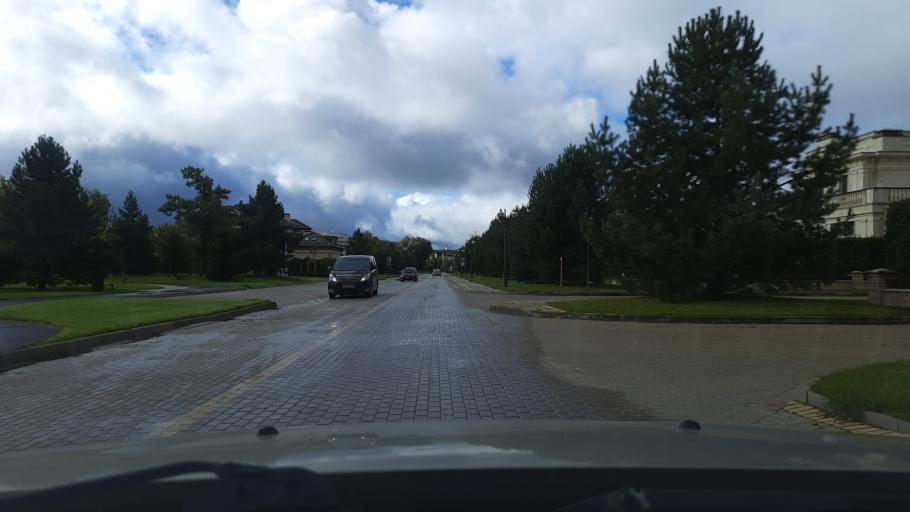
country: RU
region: Moskovskaya
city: Nikolina Gora
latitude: 55.7771
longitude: 37.0535
